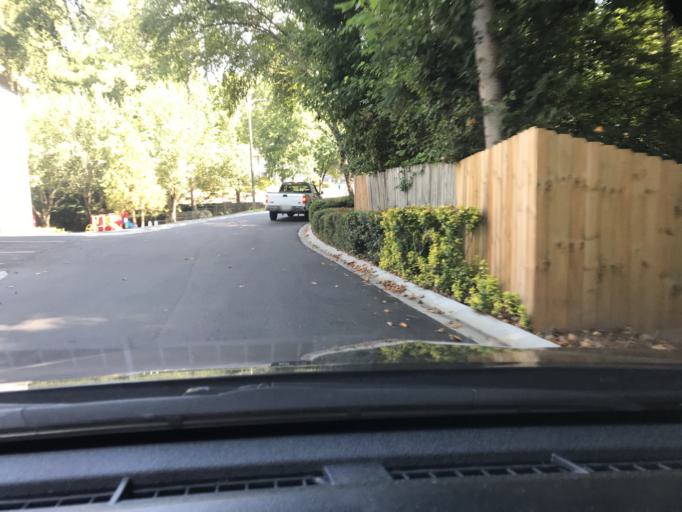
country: US
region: Georgia
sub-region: DeKalb County
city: Tucker
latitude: 33.8937
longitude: -84.2300
